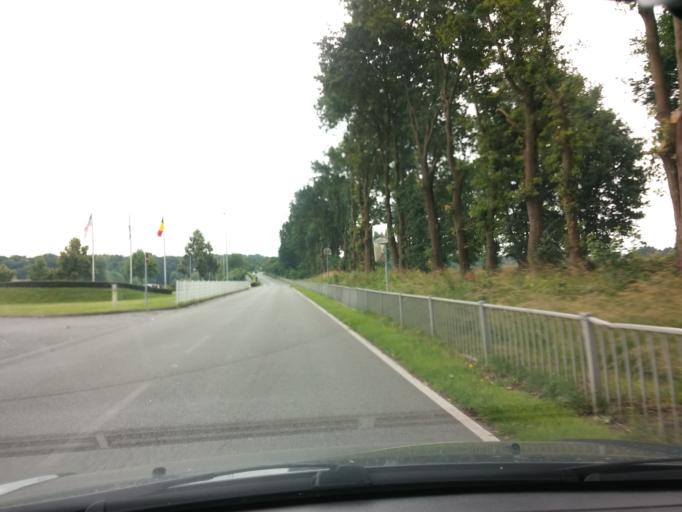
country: DE
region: North Rhine-Westphalia
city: Dorsten
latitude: 51.6209
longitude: 6.9715
